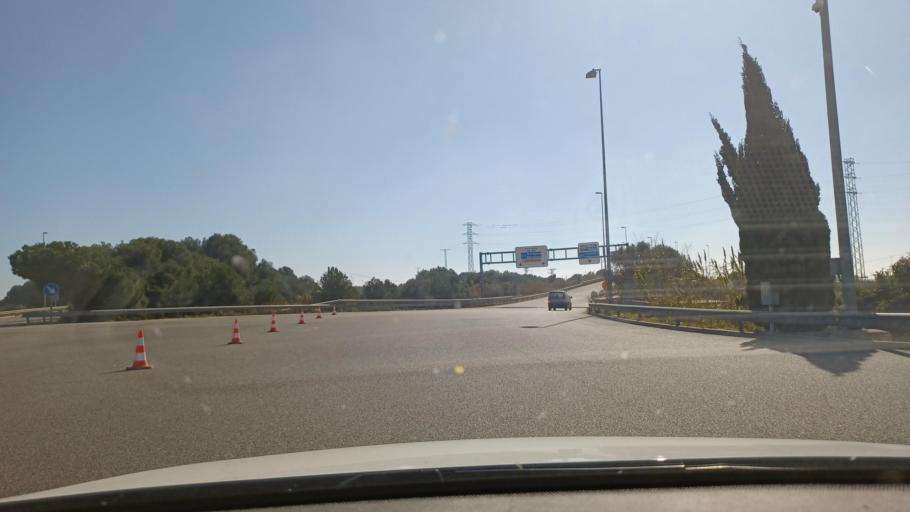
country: ES
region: Catalonia
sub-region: Provincia de Tarragona
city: Vila-seca
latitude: 41.1075
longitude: 1.1311
